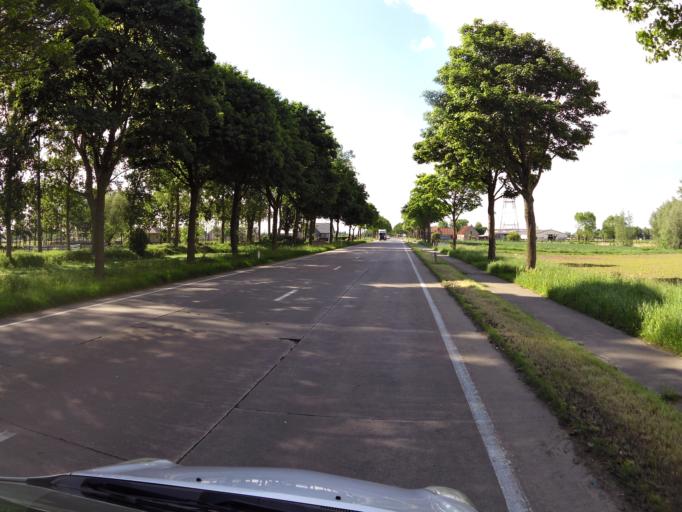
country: BE
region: Flanders
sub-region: Provincie West-Vlaanderen
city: Alveringem
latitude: 50.9393
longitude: 2.7299
